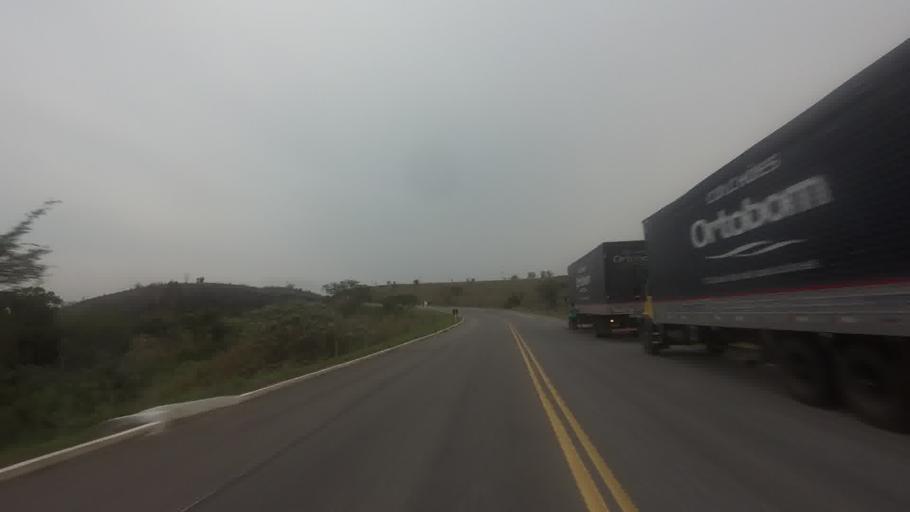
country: BR
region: Minas Gerais
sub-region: Recreio
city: Recreio
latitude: -21.6717
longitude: -42.3913
